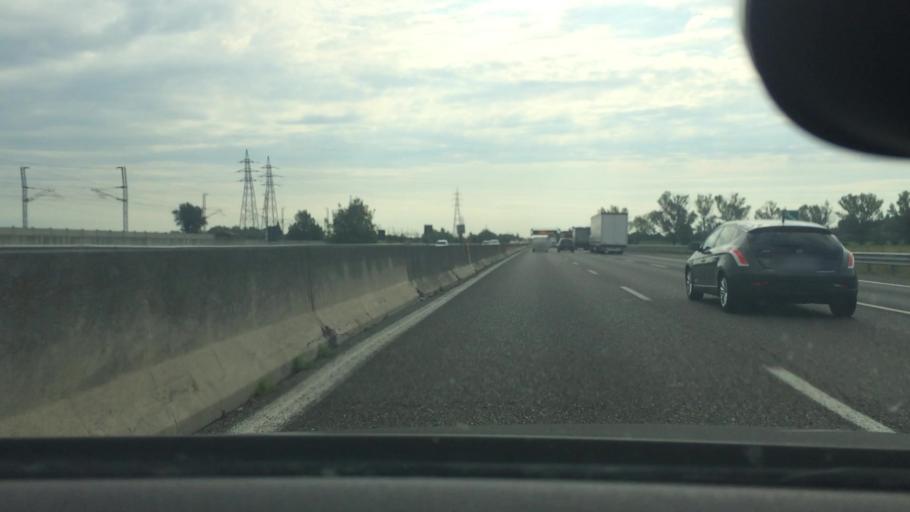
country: IT
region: Emilia-Romagna
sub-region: Provincia di Parma
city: Fidenza
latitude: 44.8920
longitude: 10.0711
